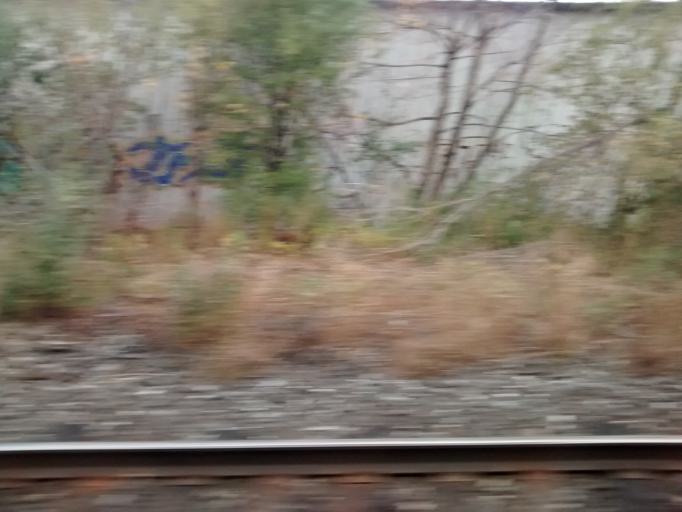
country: CA
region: Ontario
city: Burlington
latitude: 43.3635
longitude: -79.7776
